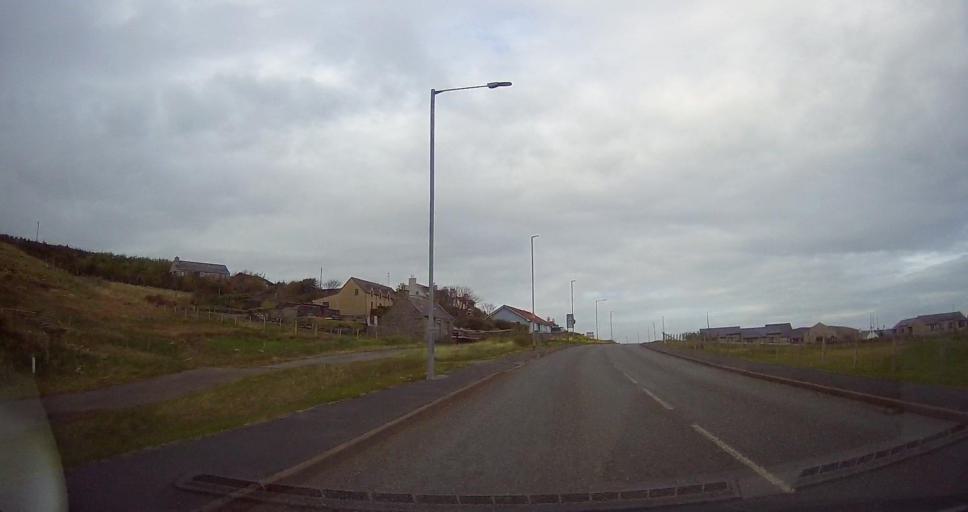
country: GB
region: Scotland
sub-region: Shetland Islands
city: Sandwick
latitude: 60.0436
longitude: -1.2293
